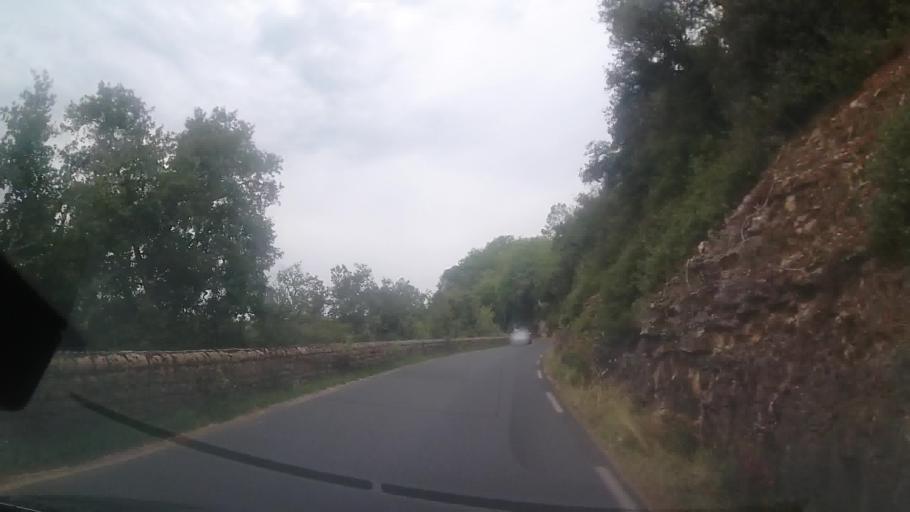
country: FR
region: Aquitaine
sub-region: Departement de la Dordogne
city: Carsac-Aillac
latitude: 44.8438
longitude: 1.2624
